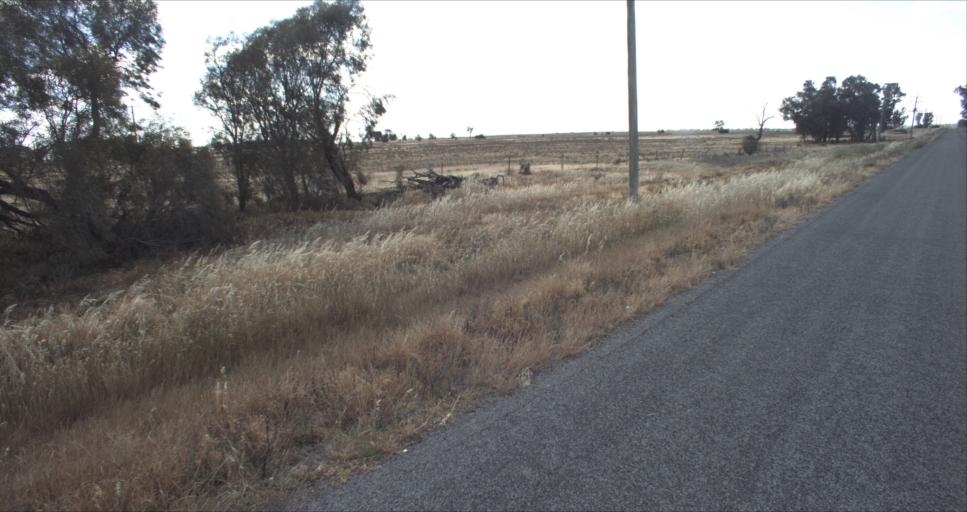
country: AU
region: New South Wales
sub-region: Leeton
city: Leeton
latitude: -34.4874
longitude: 146.2479
